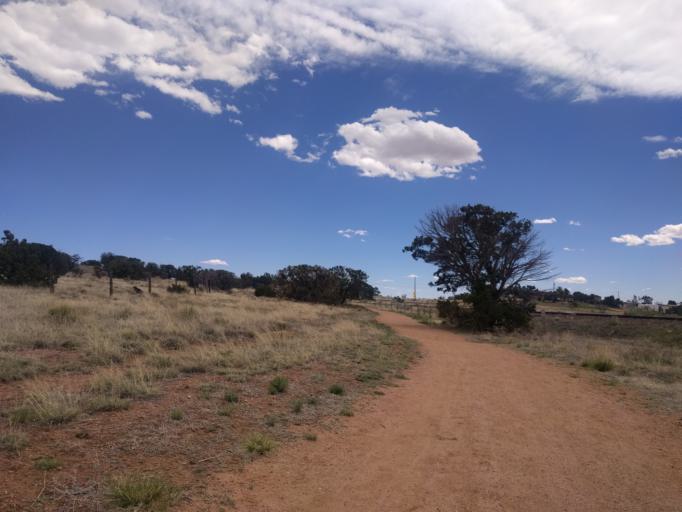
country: US
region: New Mexico
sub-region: Santa Fe County
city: Agua Fria
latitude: 35.6243
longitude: -105.9661
